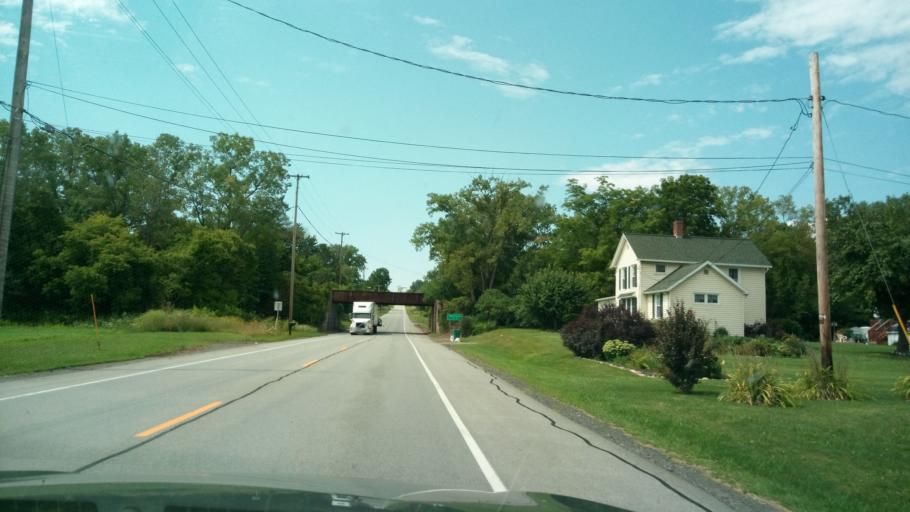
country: US
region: New York
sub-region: Livingston County
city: Geneseo
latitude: 42.8309
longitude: -77.8997
